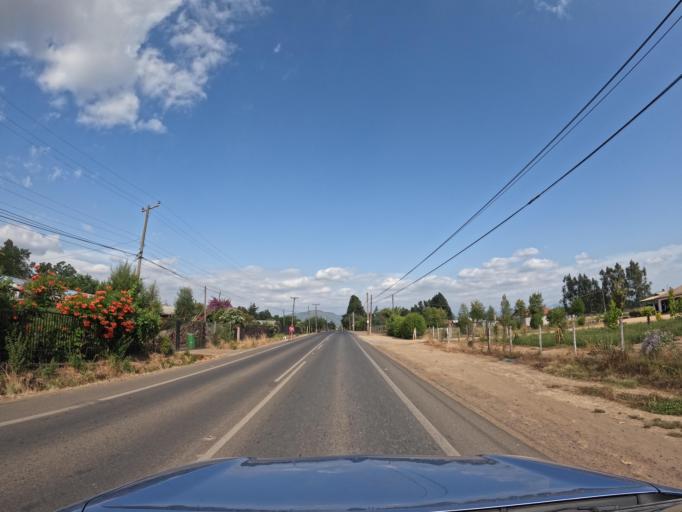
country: CL
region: Maule
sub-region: Provincia de Curico
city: Molina
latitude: -35.2763
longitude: -71.2864
